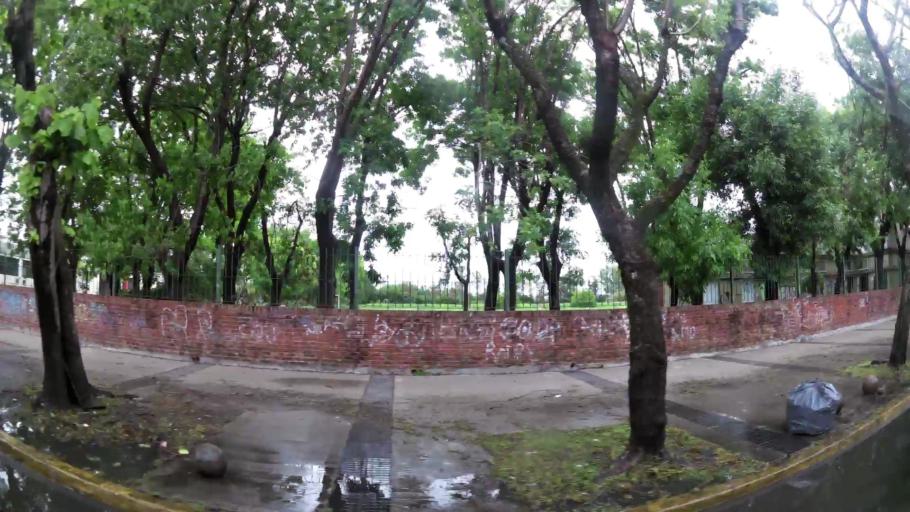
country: AR
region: Buenos Aires
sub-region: Partido de Lanus
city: Lanus
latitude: -34.7154
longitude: -58.3855
